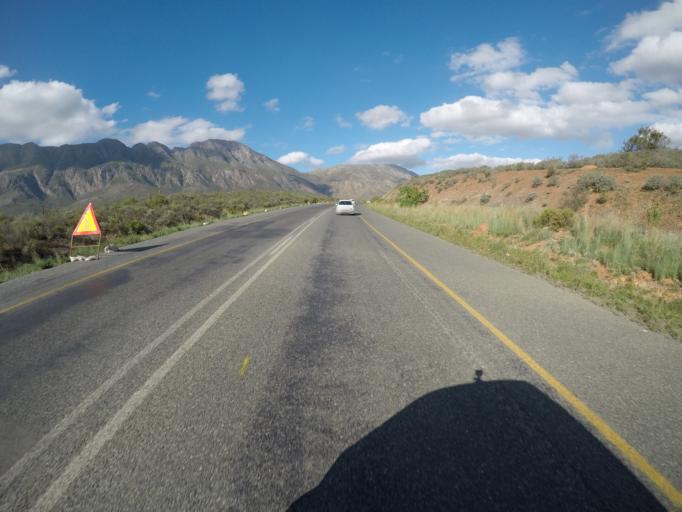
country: ZA
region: Western Cape
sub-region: Cape Winelands District Municipality
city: Ashton
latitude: -33.8659
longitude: 20.1250
